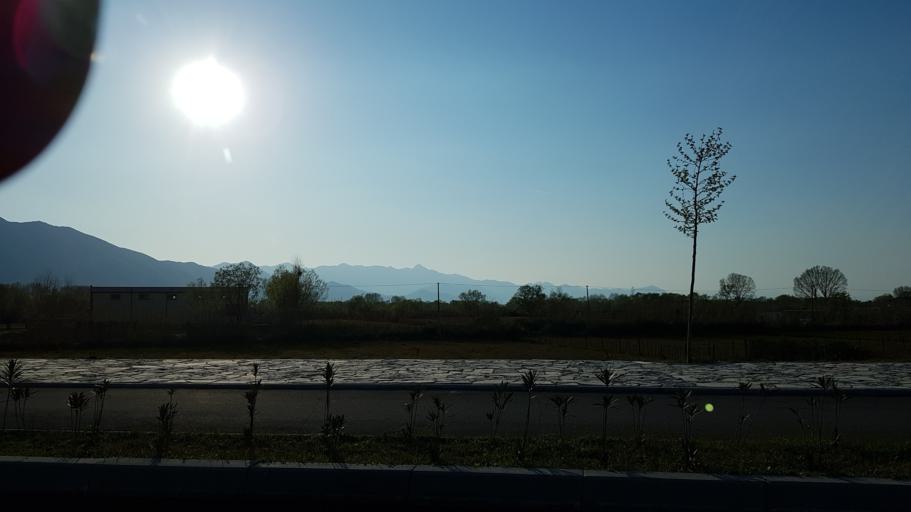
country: AL
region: Shkoder
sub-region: Rrethi i Shkodres
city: Shkoder
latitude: 42.0737
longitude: 19.4898
